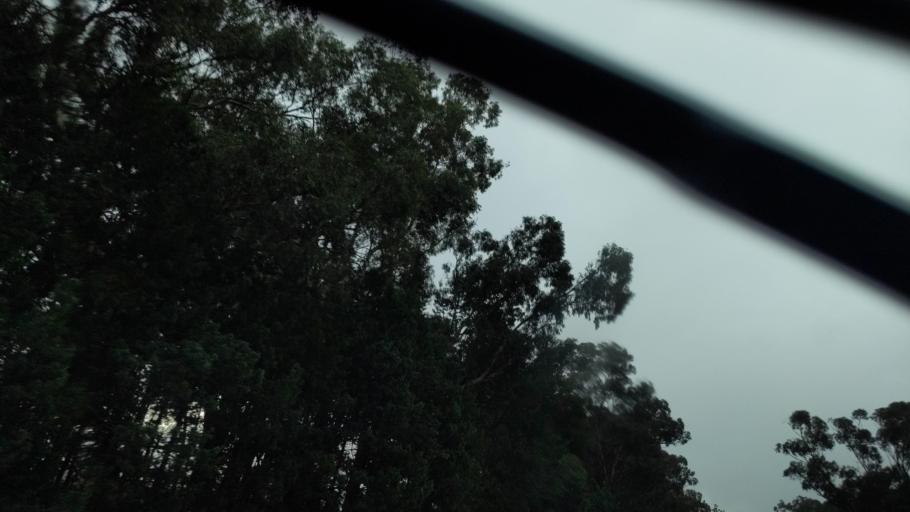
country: AU
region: New South Wales
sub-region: Coolamon
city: Coolamon
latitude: -34.8961
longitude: 147.2666
